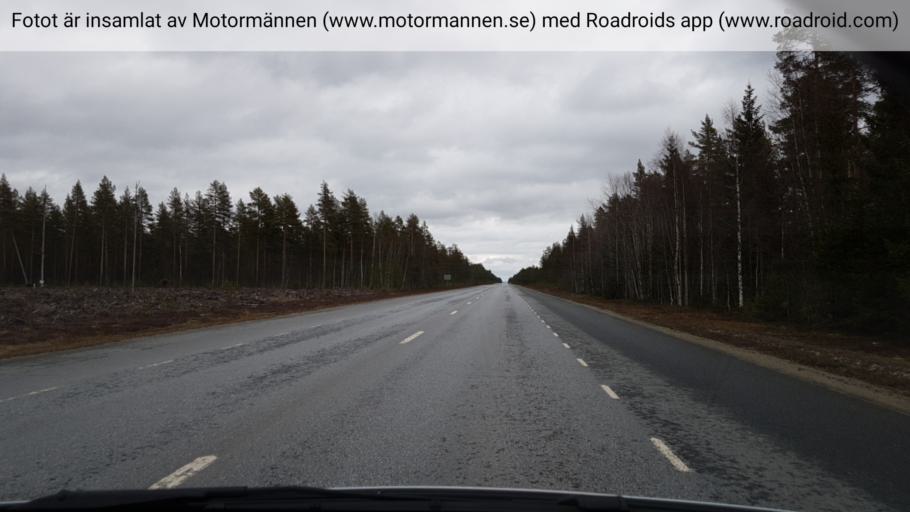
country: SE
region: Vaesterbotten
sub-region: Bjurholms Kommun
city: Bjurholm
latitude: 63.9345
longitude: 18.9539
